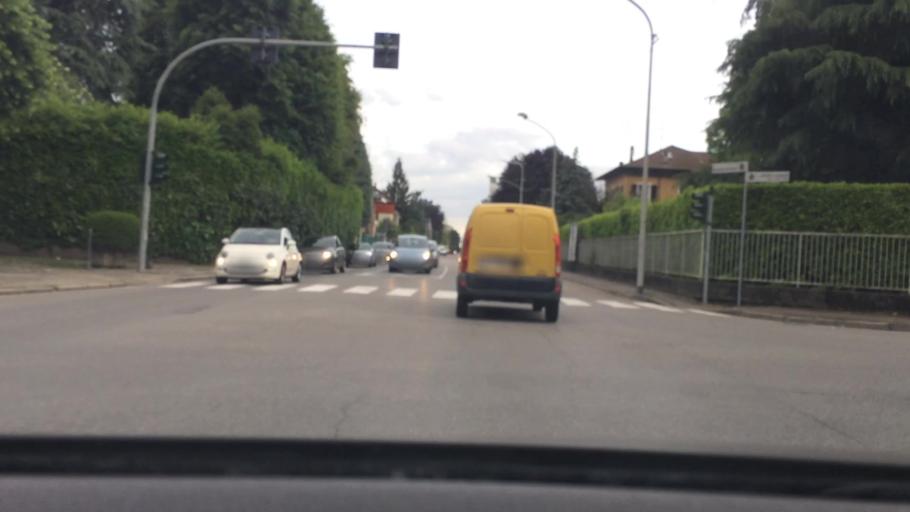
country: IT
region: Lombardy
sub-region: Provincia di Monza e Brianza
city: Barlassina
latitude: 45.6543
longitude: 9.1302
